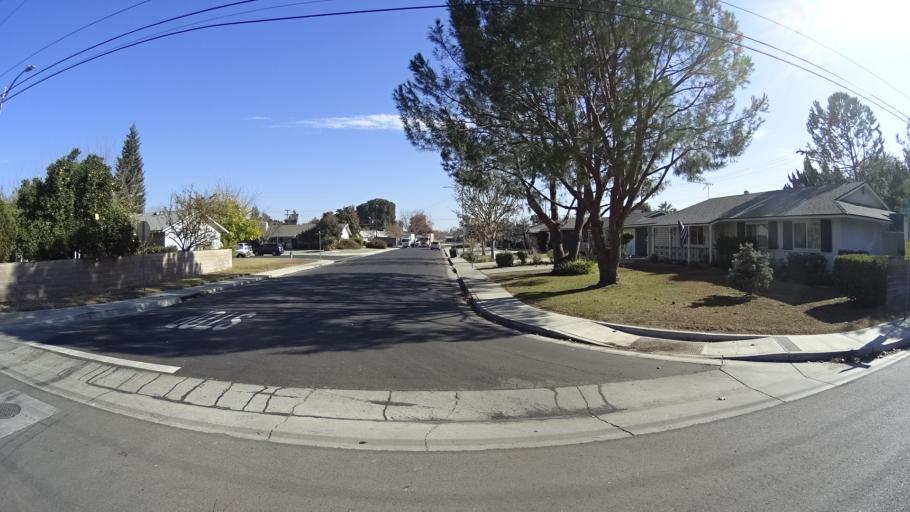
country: US
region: California
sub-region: Kern County
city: Greenacres
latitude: 35.3456
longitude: -119.0738
